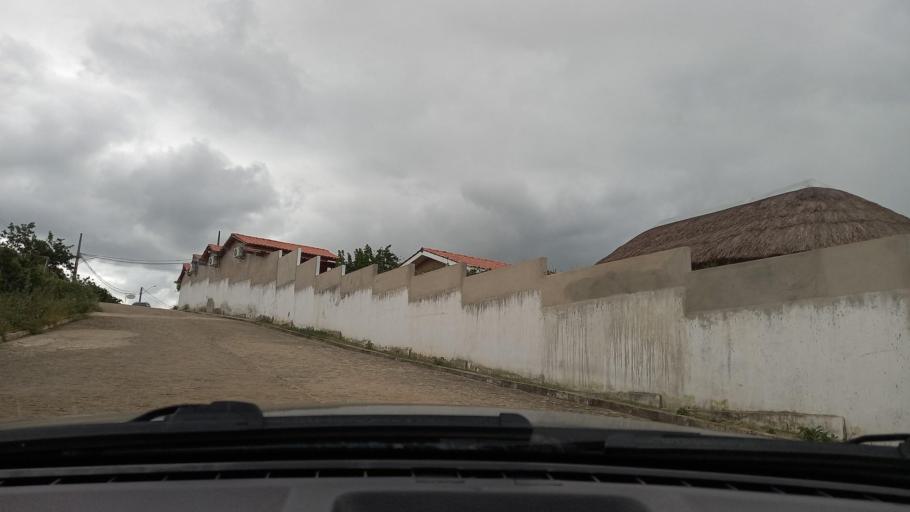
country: BR
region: Sergipe
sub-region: Caninde De Sao Francisco
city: Caninde de Sao Francisco
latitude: -9.6231
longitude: -37.7540
